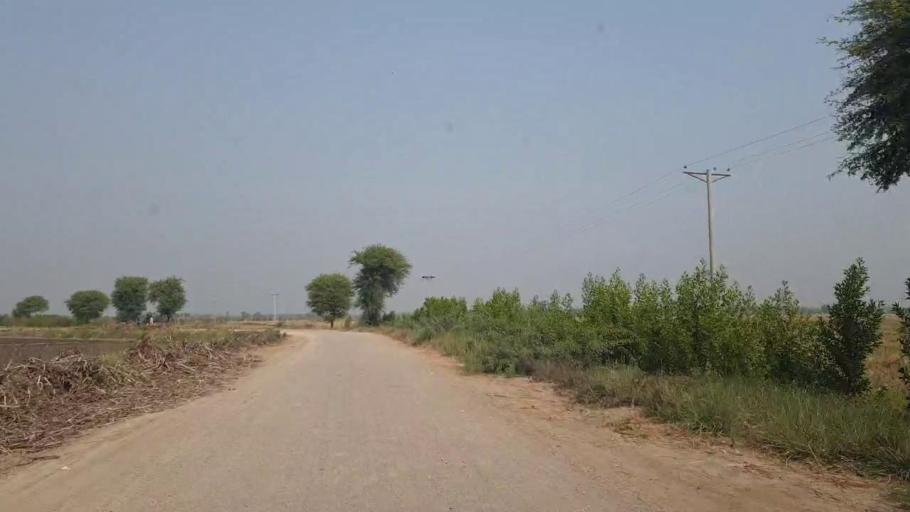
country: PK
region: Sindh
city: Matli
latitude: 25.1479
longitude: 68.7298
